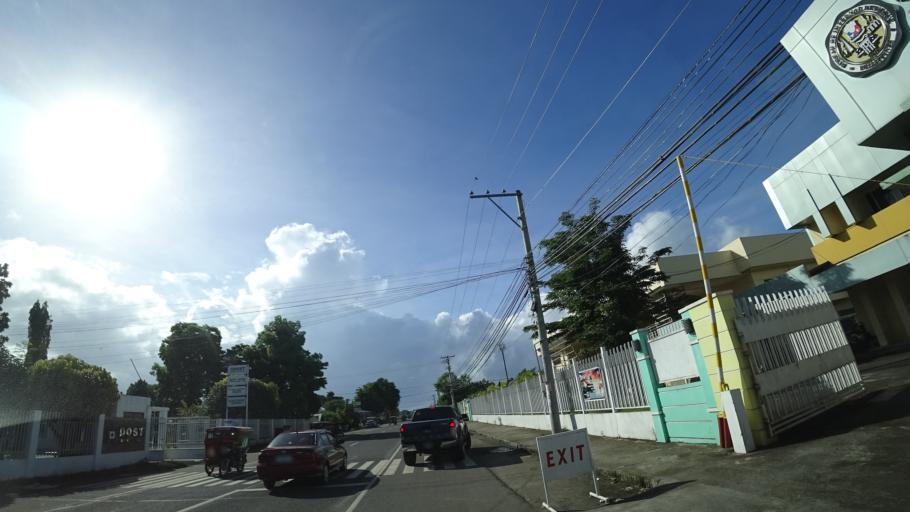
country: PH
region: Eastern Visayas
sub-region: Province of Leyte
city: Pawing
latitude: 11.1789
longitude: 125.0033
